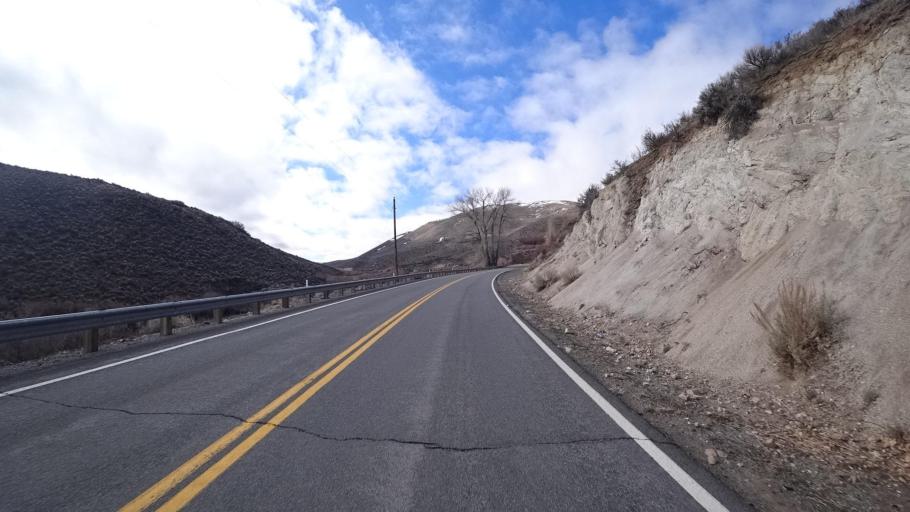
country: US
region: Nevada
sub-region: Washoe County
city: Cold Springs
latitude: 39.8323
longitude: -119.9376
